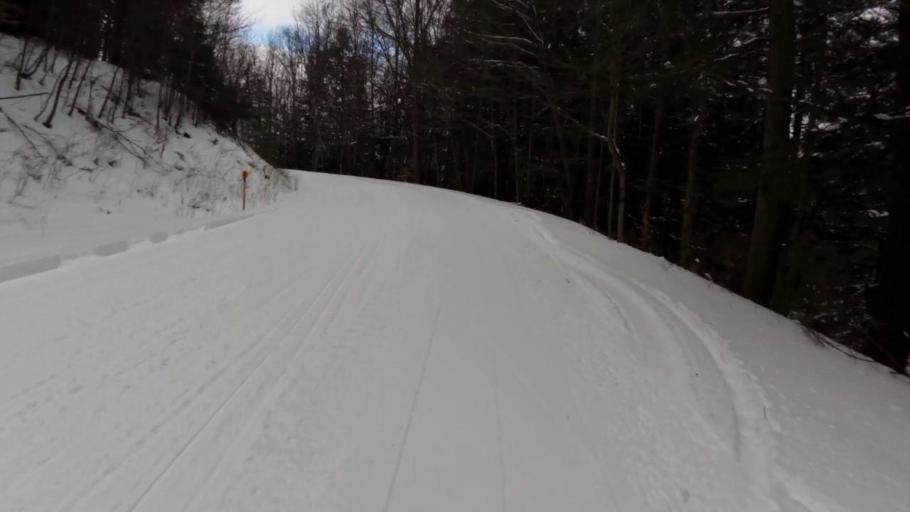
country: US
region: New York
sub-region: Cattaraugus County
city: Salamanca
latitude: 42.0671
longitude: -78.7621
